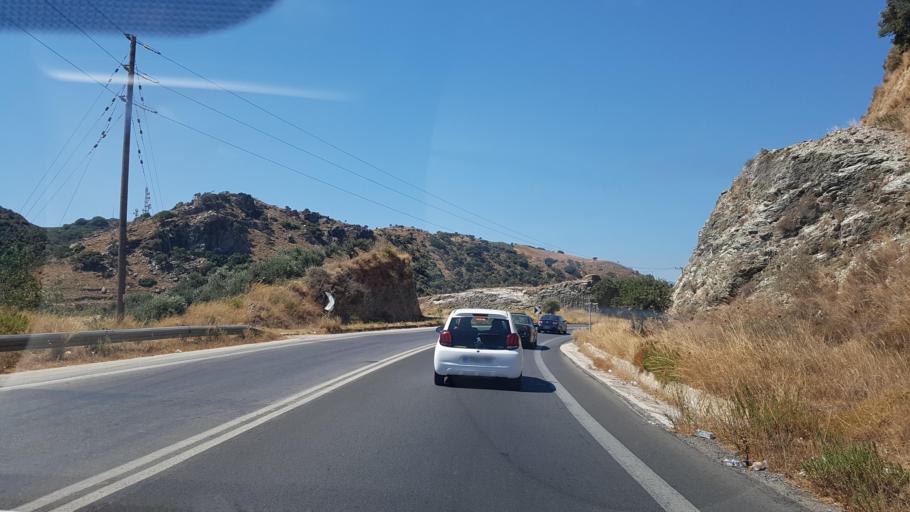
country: GR
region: Crete
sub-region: Nomos Chanias
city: Kolympari
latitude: 35.5173
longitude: 23.7439
